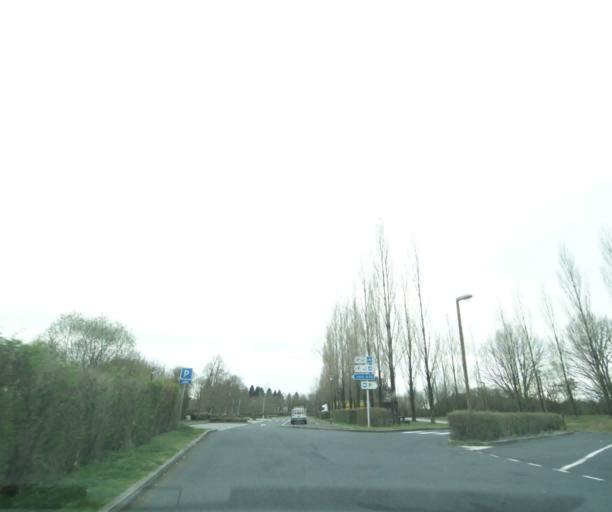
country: FR
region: Limousin
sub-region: Departement de la Correze
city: Vigeois
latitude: 45.3605
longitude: 1.5691
